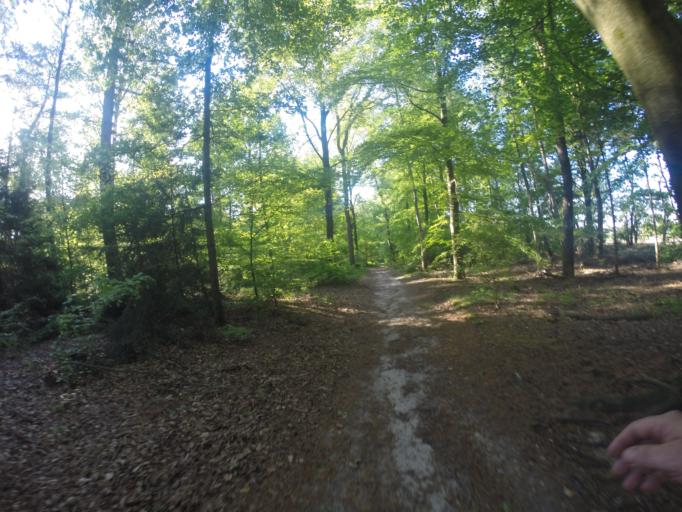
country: NL
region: Gelderland
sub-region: Gemeente Montferland
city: s-Heerenberg
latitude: 51.8874
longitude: 6.2362
